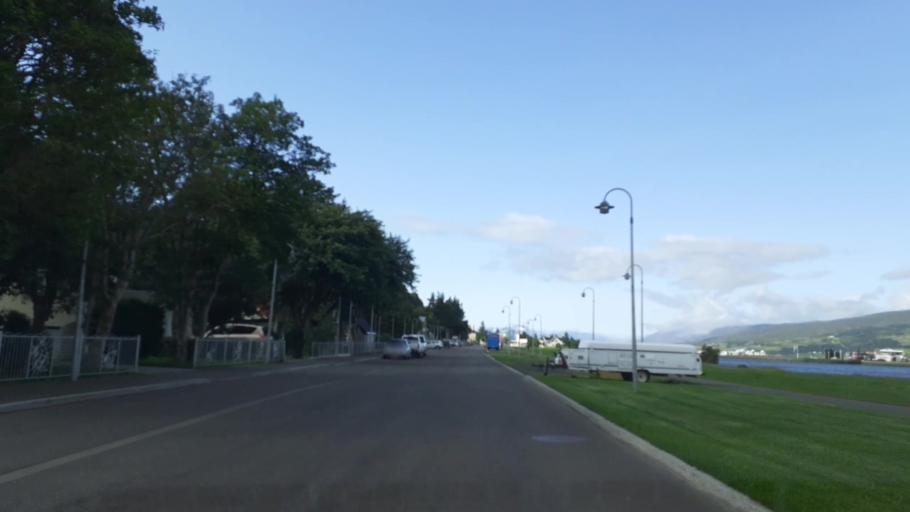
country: IS
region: Northeast
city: Akureyri
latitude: 65.6653
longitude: -18.0843
